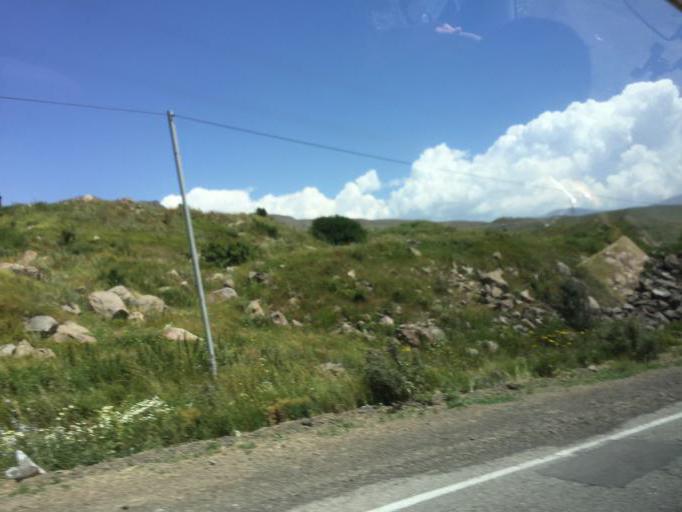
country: AM
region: Vayots' Dzori Marz
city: Jermuk
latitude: 39.6848
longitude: 45.7241
